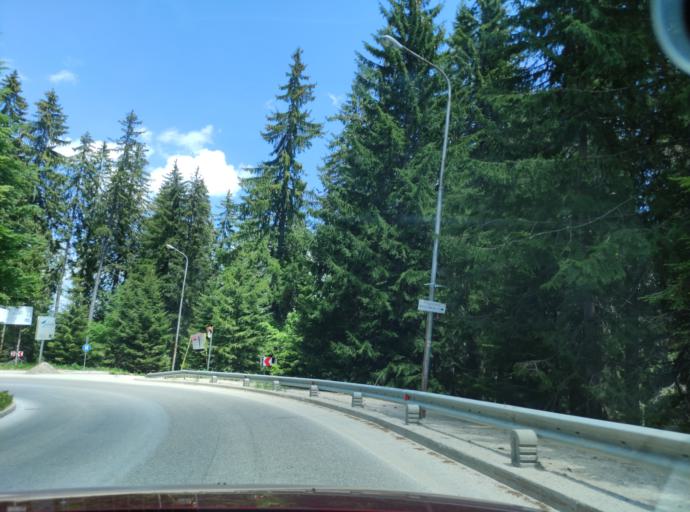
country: BG
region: Smolyan
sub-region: Obshtina Smolyan
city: Smolyan
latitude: 41.6464
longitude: 24.6989
